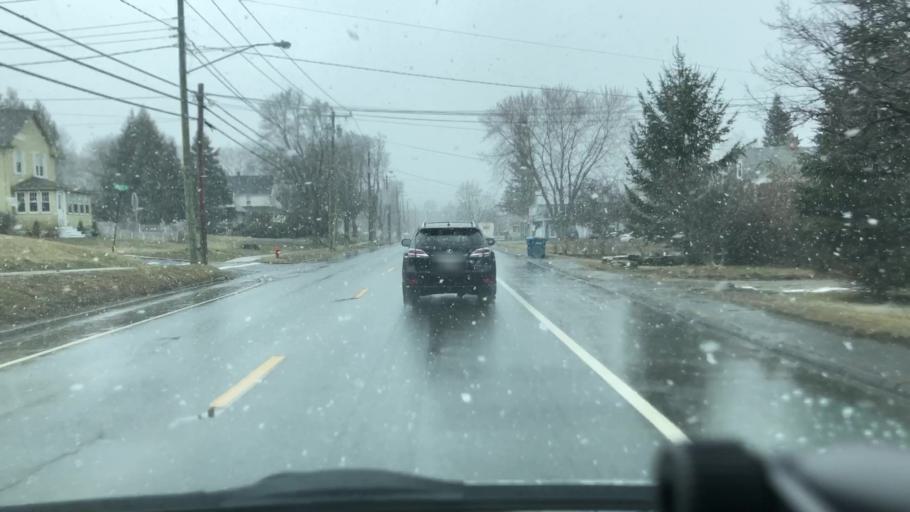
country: US
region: Massachusetts
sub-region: Berkshire County
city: Dalton
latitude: 42.4782
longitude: -73.1572
